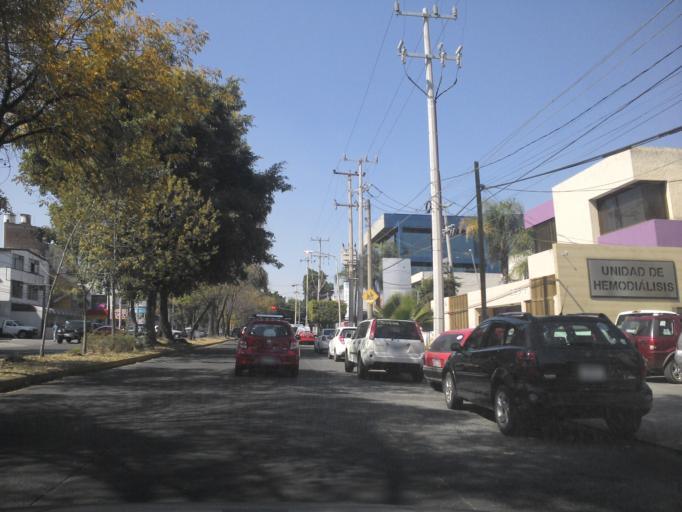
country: MX
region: Jalisco
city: Guadalajara
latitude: 20.6766
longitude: -103.3901
